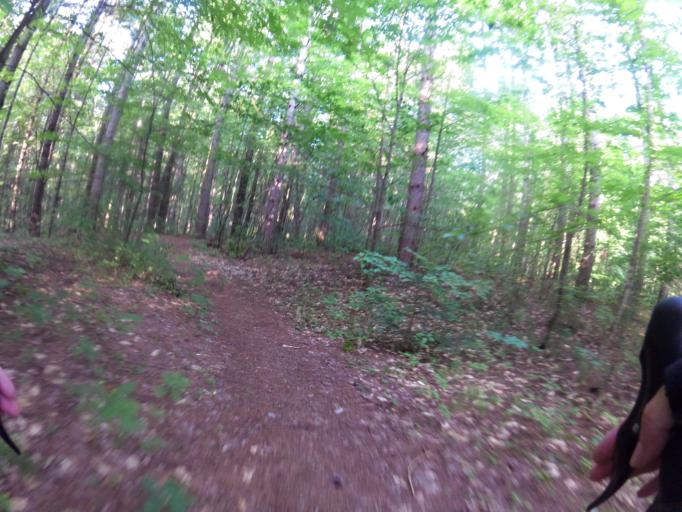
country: CA
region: Ontario
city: Ottawa
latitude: 45.3198
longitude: -75.7267
